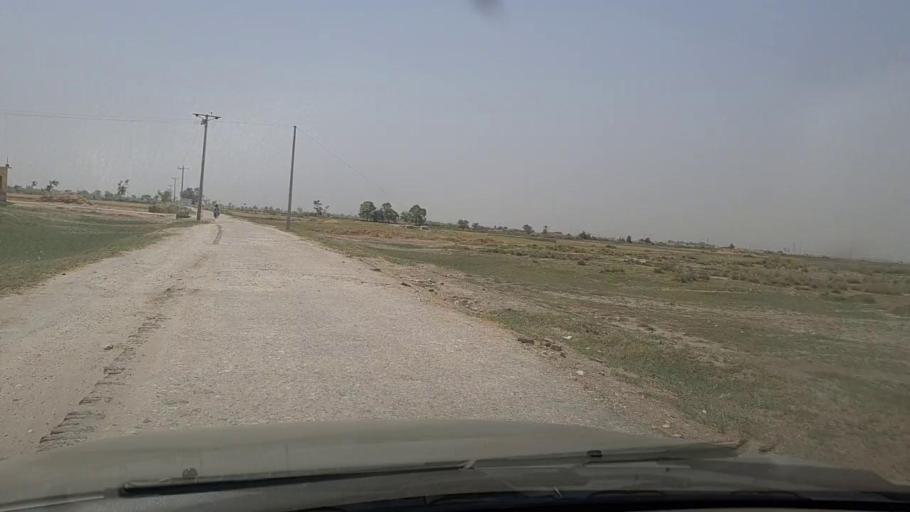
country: PK
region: Sindh
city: Miro Khan
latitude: 27.7676
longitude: 68.1417
